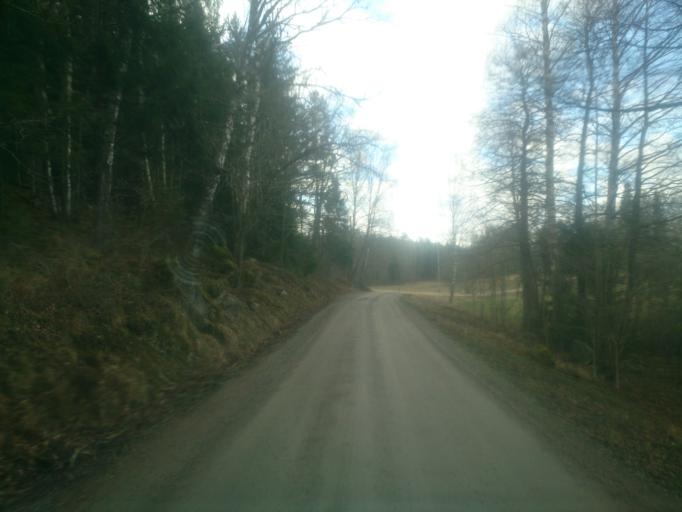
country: SE
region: OEstergoetland
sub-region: Atvidabergs Kommun
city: Atvidaberg
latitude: 58.1952
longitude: 16.1534
